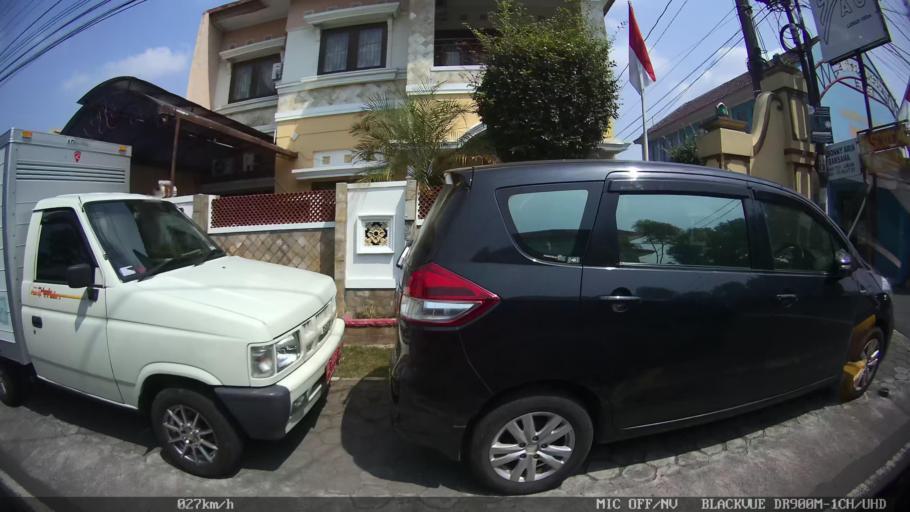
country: ID
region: Daerah Istimewa Yogyakarta
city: Yogyakarta
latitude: -7.8066
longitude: 110.3945
